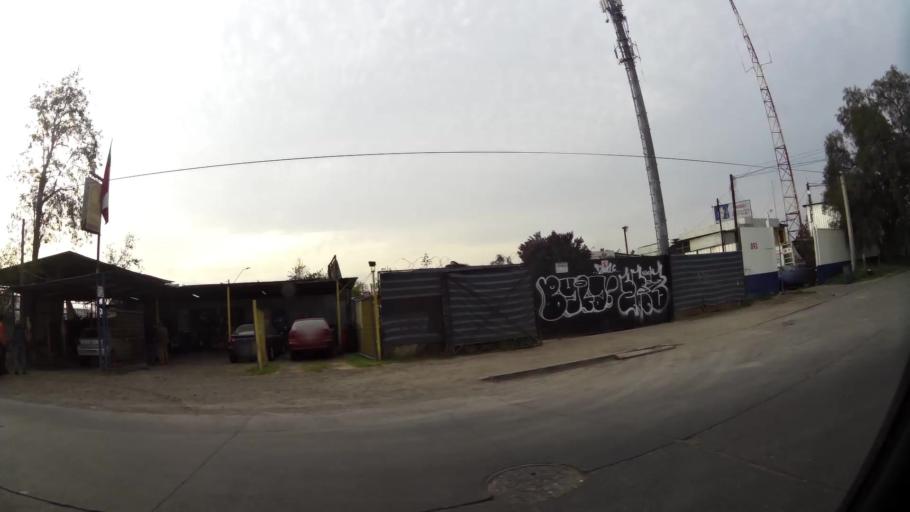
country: CL
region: Santiago Metropolitan
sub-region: Provincia de Maipo
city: San Bernardo
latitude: -33.5282
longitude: -70.7693
